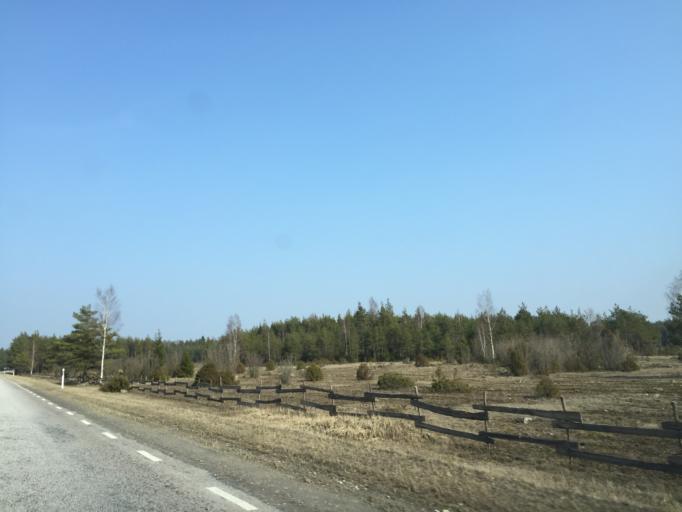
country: EE
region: Saare
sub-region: Kuressaare linn
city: Kuressaare
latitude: 58.3805
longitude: 22.7360
